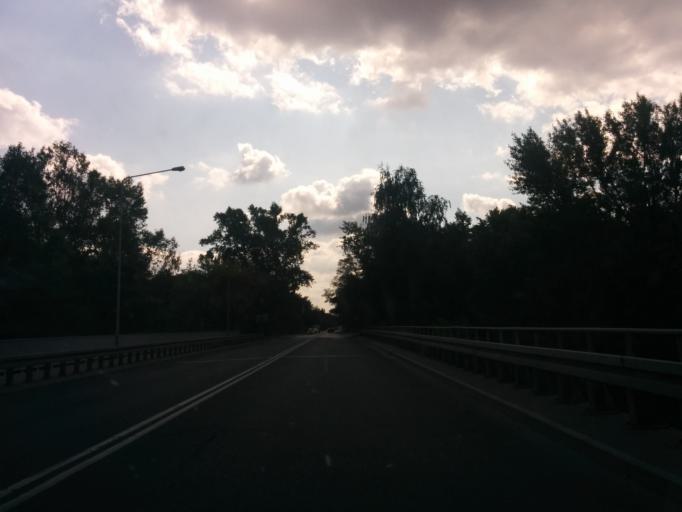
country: PL
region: Masovian Voivodeship
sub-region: Warszawa
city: Bialoleka
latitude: 52.3145
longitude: 21.0009
